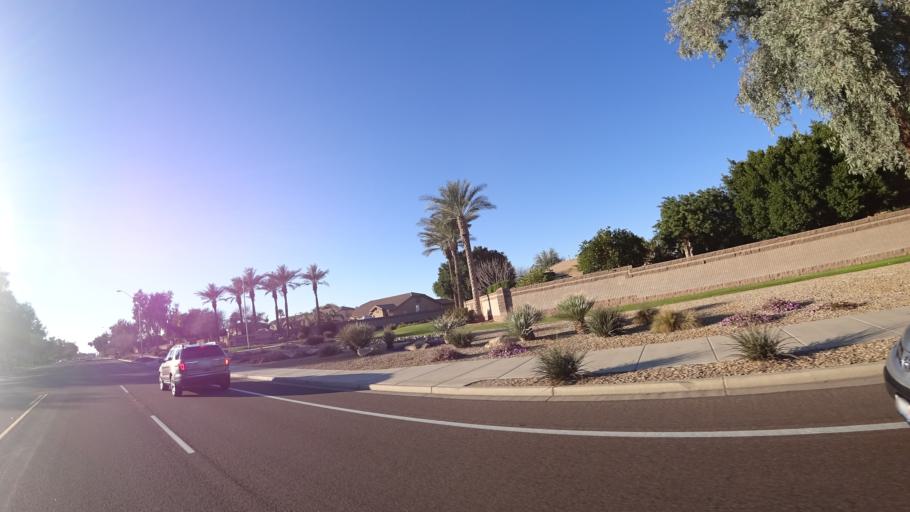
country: US
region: Arizona
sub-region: Maricopa County
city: Sun City
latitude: 33.6816
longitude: -112.2308
